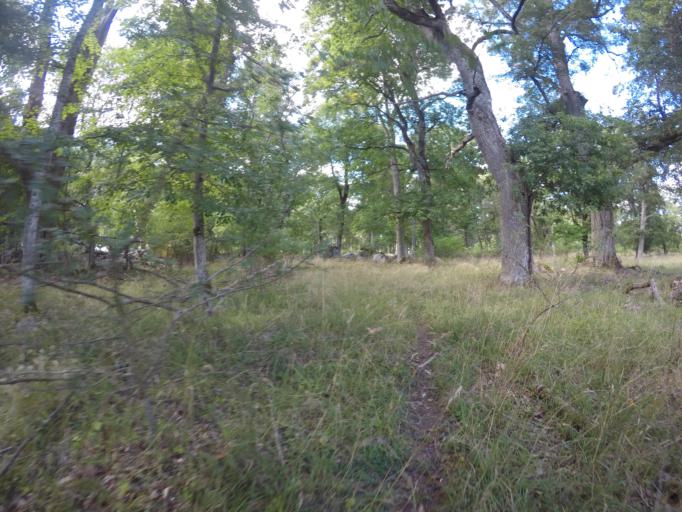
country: SE
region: Vaestmanland
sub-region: Hallstahammars Kommun
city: Kolback
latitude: 59.5014
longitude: 16.2325
